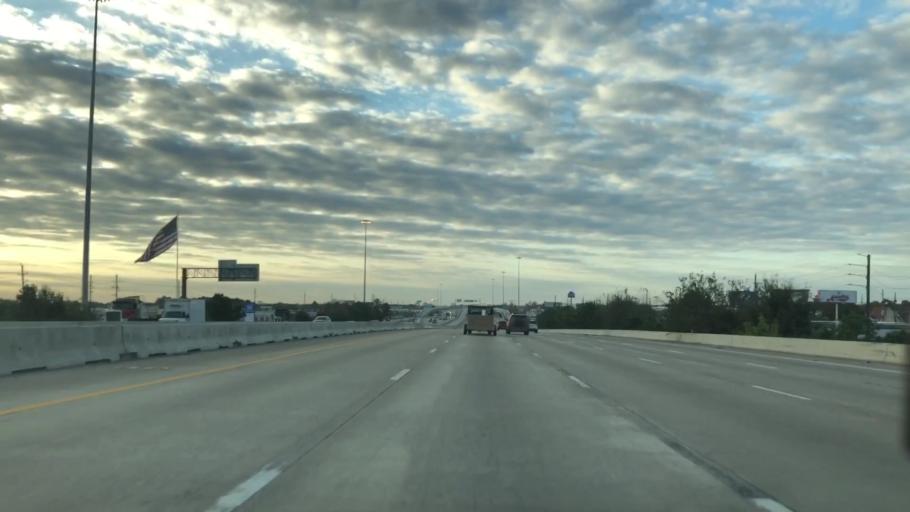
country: US
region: Texas
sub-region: Harris County
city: Spring
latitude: 30.0203
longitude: -95.4289
